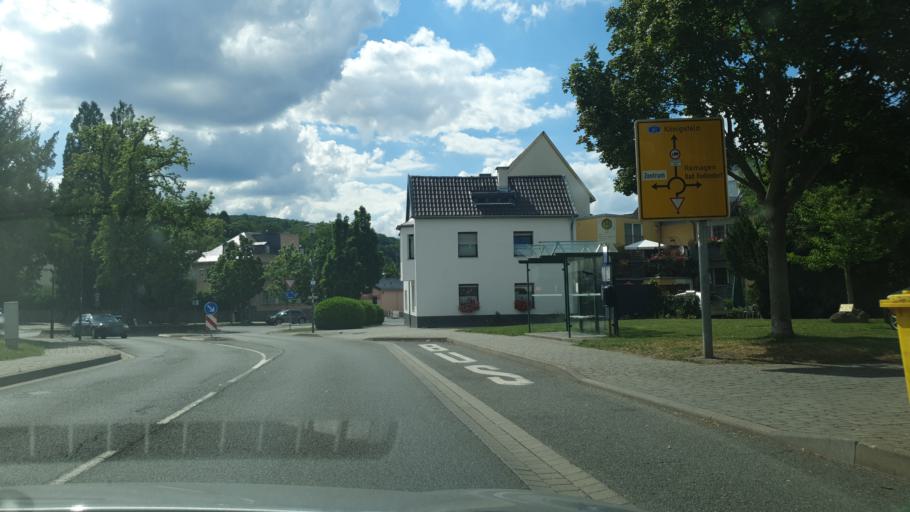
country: DE
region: Rheinland-Pfalz
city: Sinzig
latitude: 50.5459
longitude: 7.2469
